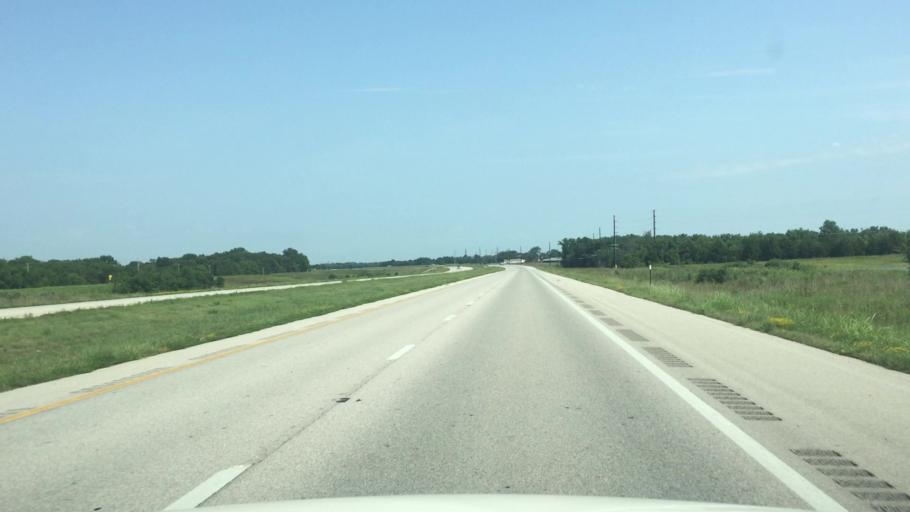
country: US
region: Kansas
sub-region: Montgomery County
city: Coffeyville
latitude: 37.0611
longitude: -95.5824
